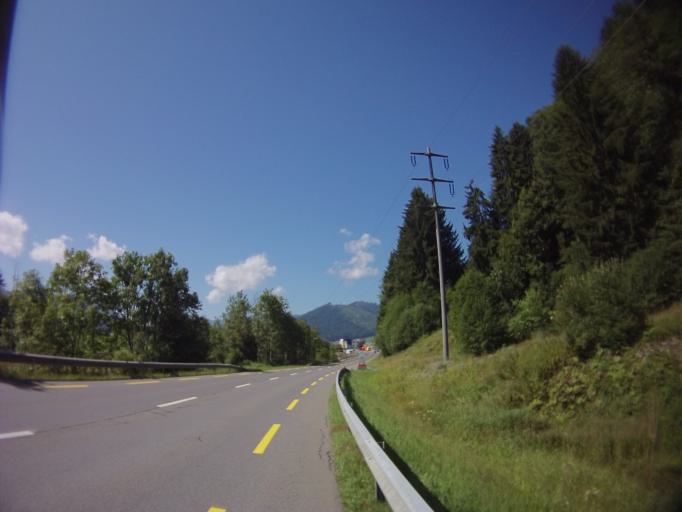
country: CH
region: Schwyz
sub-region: Bezirk Einsiedeln
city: Einsiedeln
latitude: 47.1411
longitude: 8.7490
